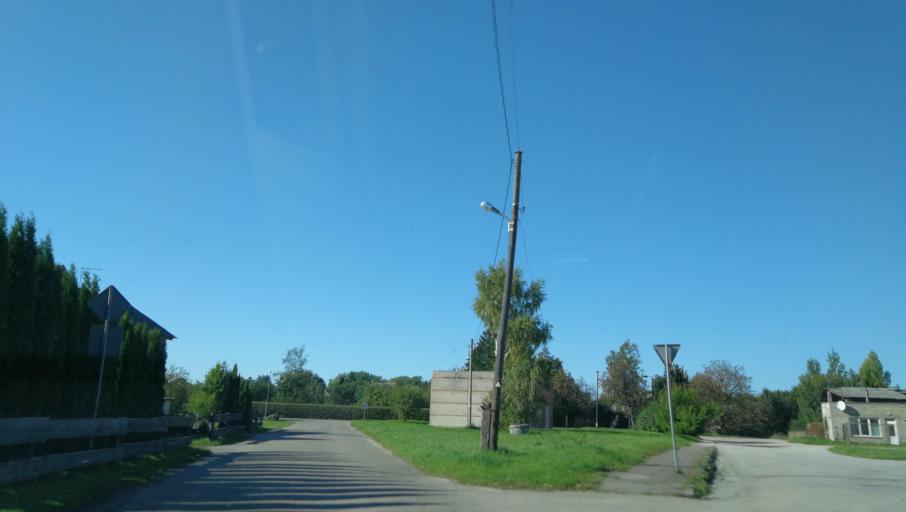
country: LV
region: Aizpute
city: Aizpute
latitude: 56.7266
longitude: 21.5929
